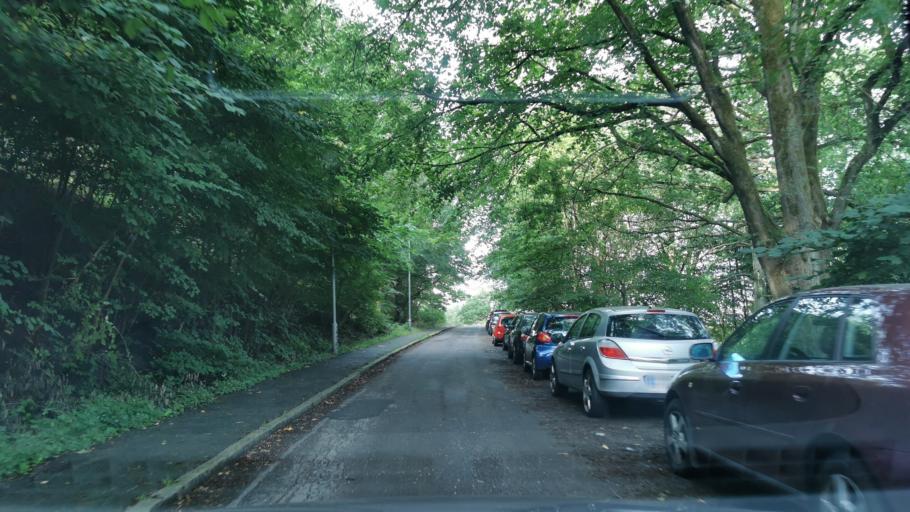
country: SE
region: Vaestra Goetaland
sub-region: Goteborg
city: Majorna
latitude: 57.6774
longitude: 11.9428
